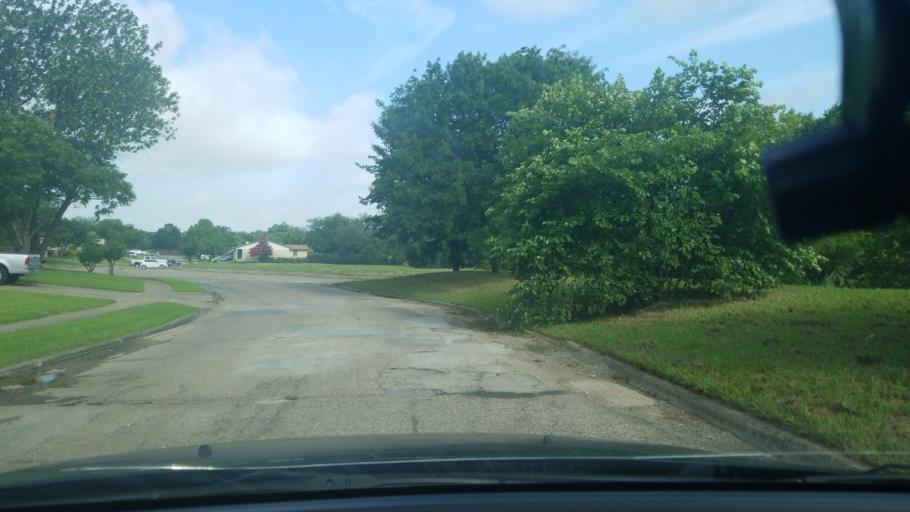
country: US
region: Texas
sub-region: Dallas County
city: Mesquite
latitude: 32.7735
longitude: -96.6313
